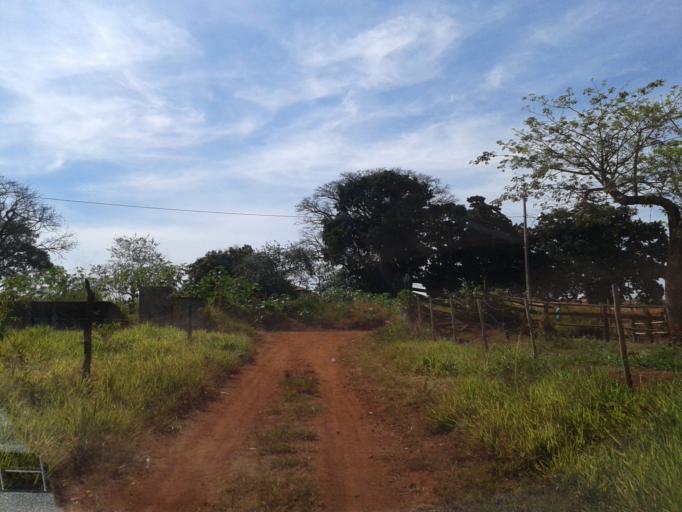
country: BR
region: Minas Gerais
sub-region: Ituiutaba
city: Ituiutaba
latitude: -18.9579
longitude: -49.4628
